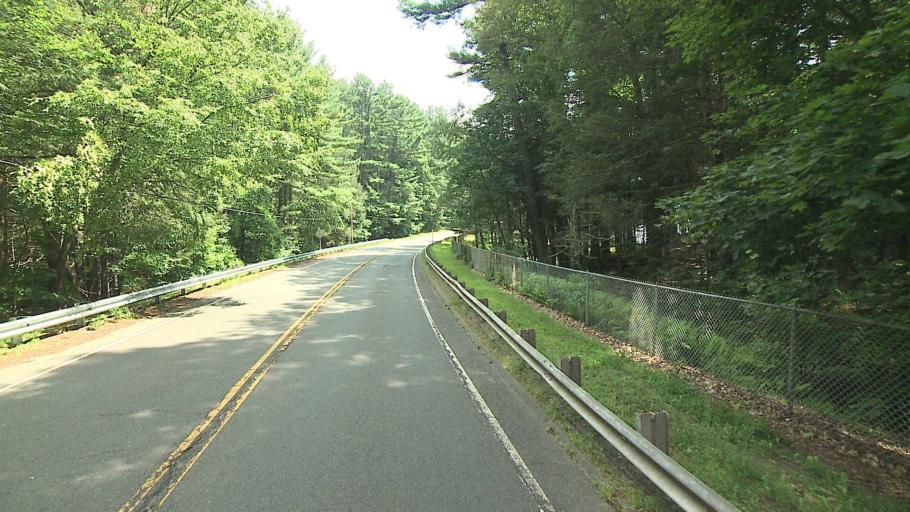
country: US
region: Connecticut
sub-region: Litchfield County
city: Thomaston
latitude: 41.6692
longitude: -73.1339
